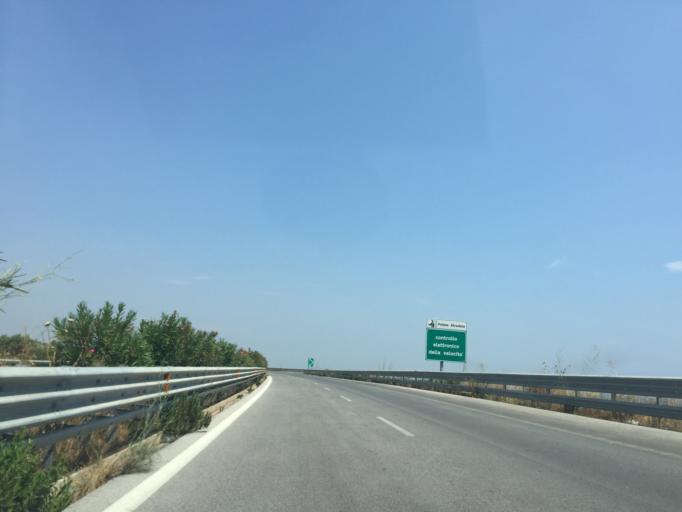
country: IT
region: Sicily
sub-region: Provincia di Siracusa
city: Avola
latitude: 36.9395
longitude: 15.1594
